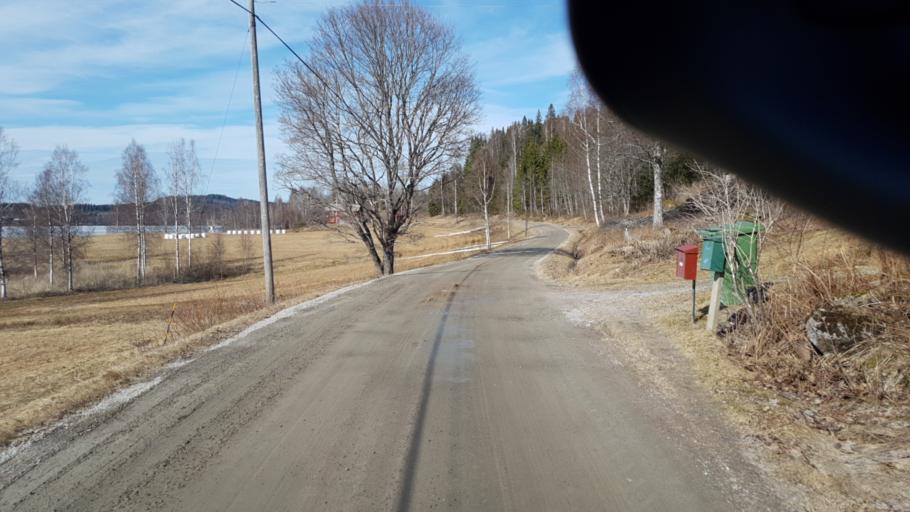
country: SE
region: Vaermland
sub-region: Arvika Kommun
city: Arvika
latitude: 59.7313
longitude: 12.8330
